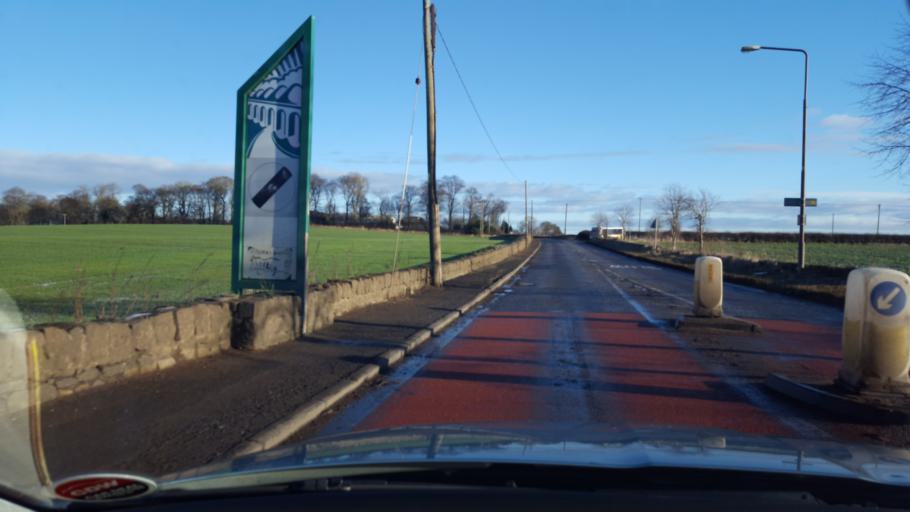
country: GB
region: Scotland
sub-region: West Lothian
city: Broxburn
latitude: 55.9614
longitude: -3.4519
